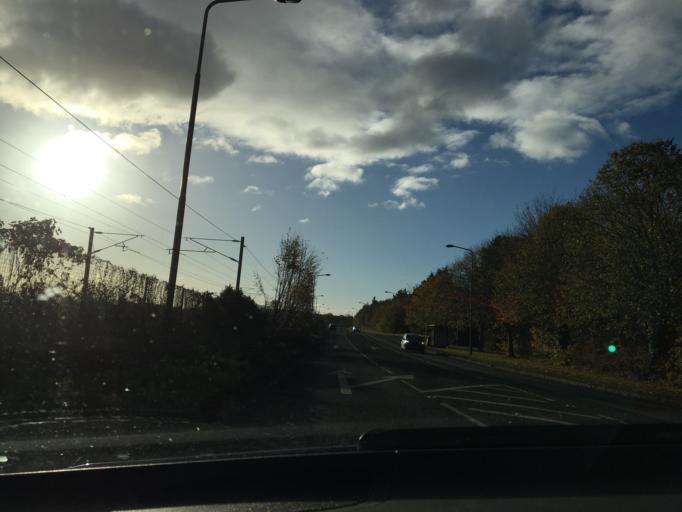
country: GB
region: Scotland
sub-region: East Lothian
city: Longniddry
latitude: 55.9710
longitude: -2.9010
